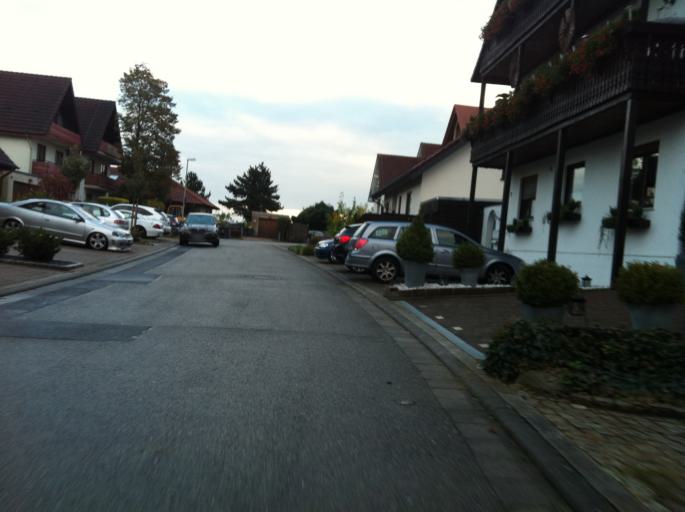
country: DE
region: Rheinland-Pfalz
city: Wackernheim
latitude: 49.9774
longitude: 8.1236
